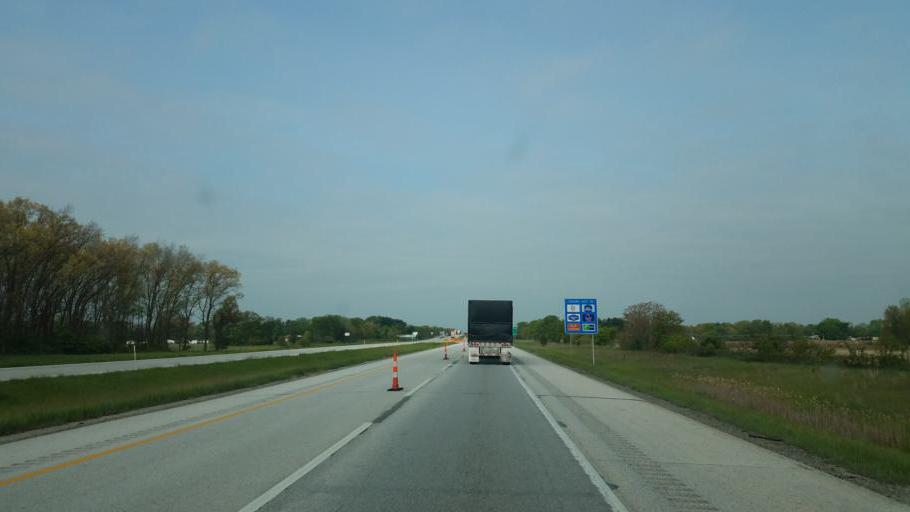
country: US
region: Indiana
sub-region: Elkhart County
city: Simonton Lake
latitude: 41.7303
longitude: -85.9374
